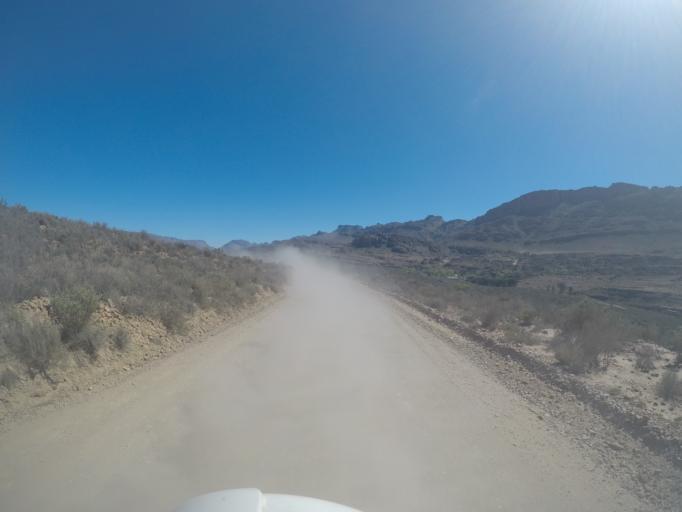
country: ZA
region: Western Cape
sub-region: West Coast District Municipality
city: Clanwilliam
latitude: -32.4964
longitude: 19.2725
